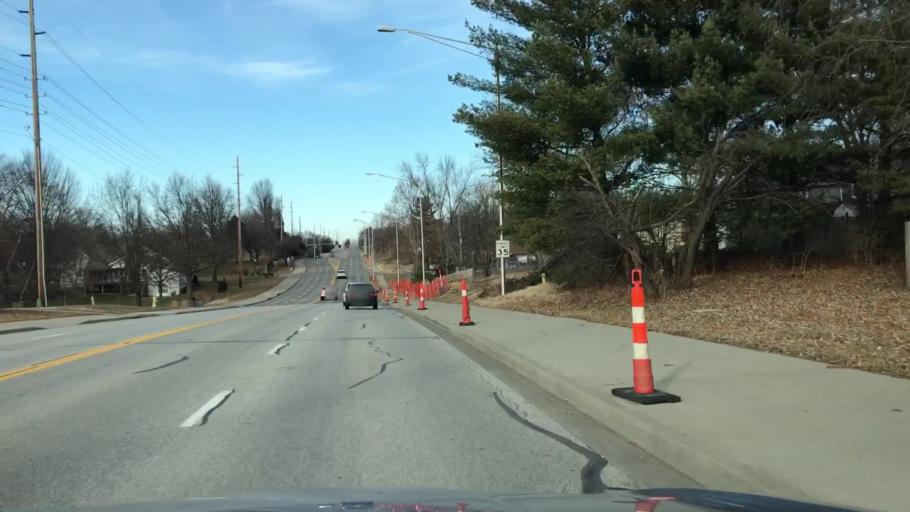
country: US
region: Missouri
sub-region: Jackson County
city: Lees Summit
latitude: 38.9087
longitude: -94.4137
